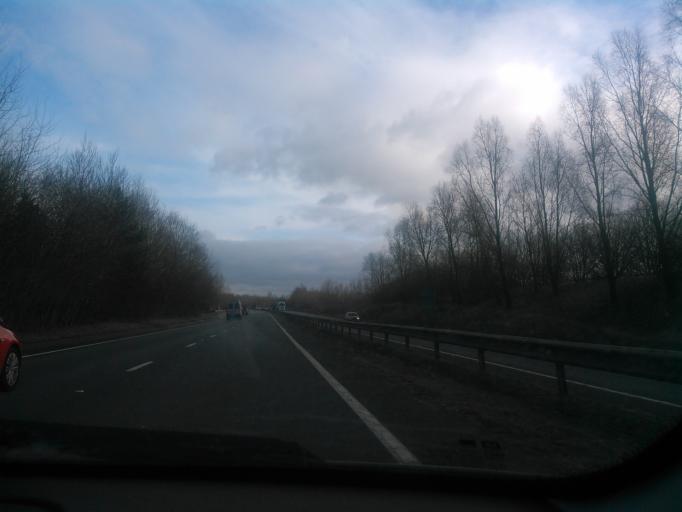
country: GB
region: England
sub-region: Derbyshire
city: Etwall
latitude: 52.8785
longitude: -1.6524
